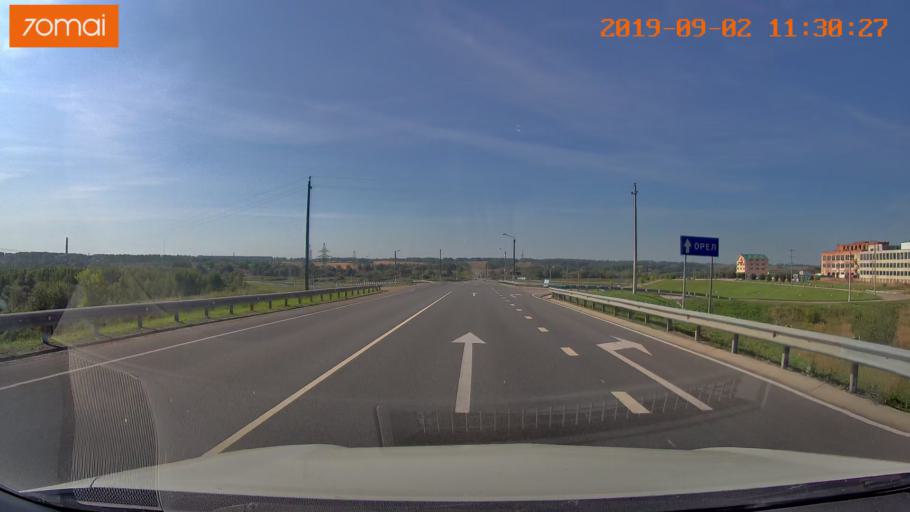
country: RU
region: Smolensk
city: Roslavl'
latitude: 53.9839
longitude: 32.8335
